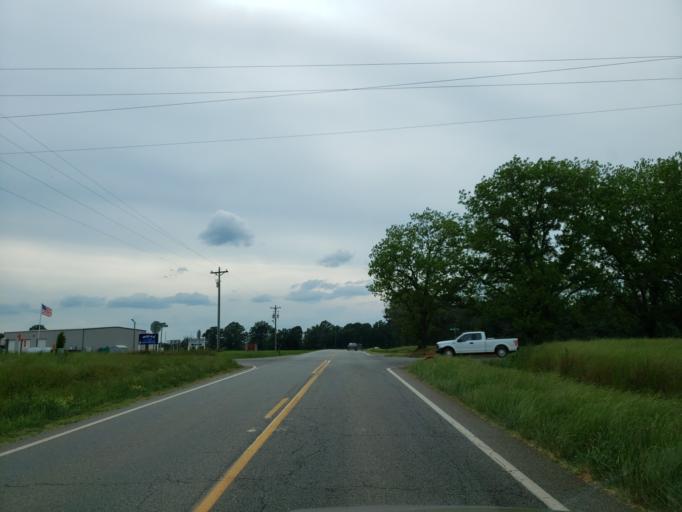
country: US
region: Georgia
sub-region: Macon County
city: Marshallville
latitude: 32.3581
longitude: -83.9391
